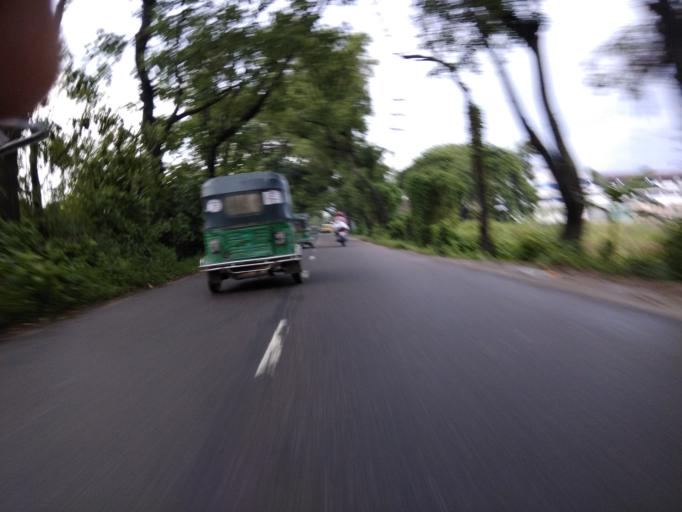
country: BD
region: Dhaka
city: Azimpur
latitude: 23.6980
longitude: 90.3359
